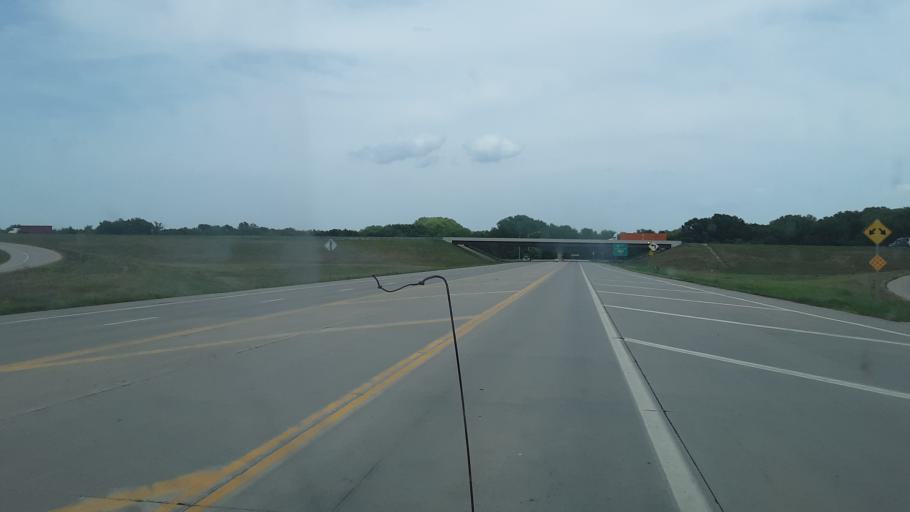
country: US
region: Kansas
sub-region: Bourbon County
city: Fort Scott
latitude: 37.8550
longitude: -94.7052
